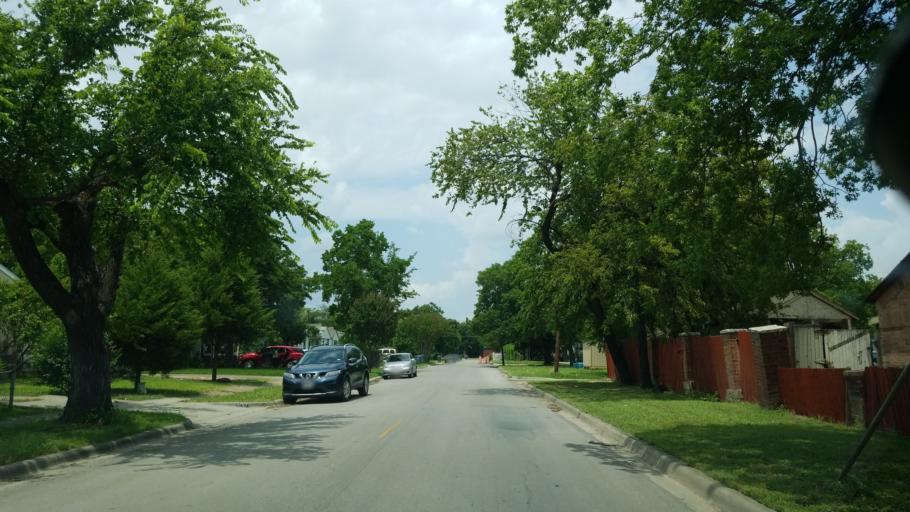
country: US
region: Texas
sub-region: Dallas County
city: Farmers Branch
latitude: 32.8733
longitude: -96.8607
